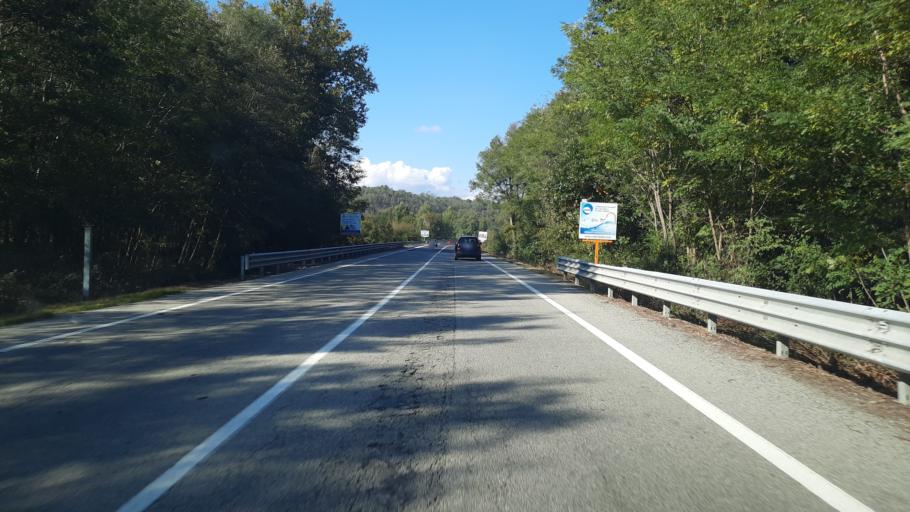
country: IT
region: Piedmont
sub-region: Provincia di Novara
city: Gargallo
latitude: 45.7314
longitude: 8.4348
